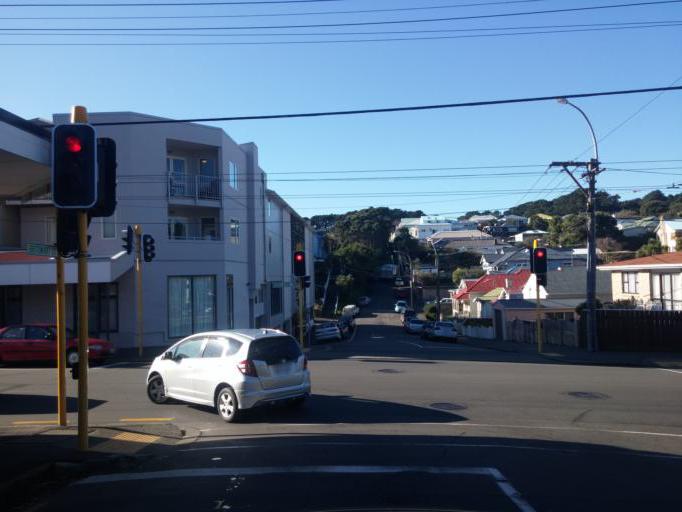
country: NZ
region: Wellington
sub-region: Wellington City
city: Brooklyn
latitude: -41.3207
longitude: 174.7750
